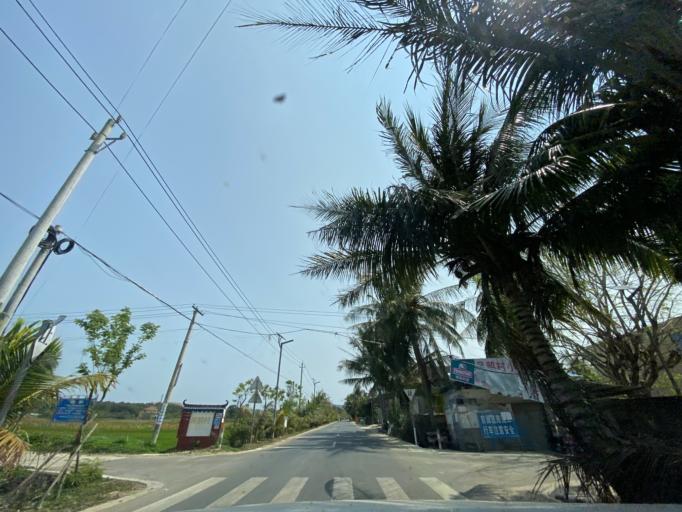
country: CN
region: Hainan
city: Yingzhou
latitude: 18.4153
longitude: 109.8146
